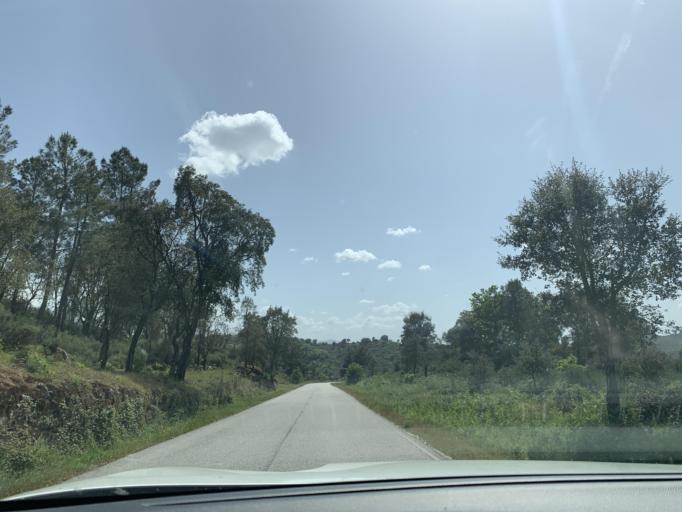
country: PT
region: Guarda
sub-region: Fornos de Algodres
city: Fornos de Algodres
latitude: 40.5728
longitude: -7.5951
